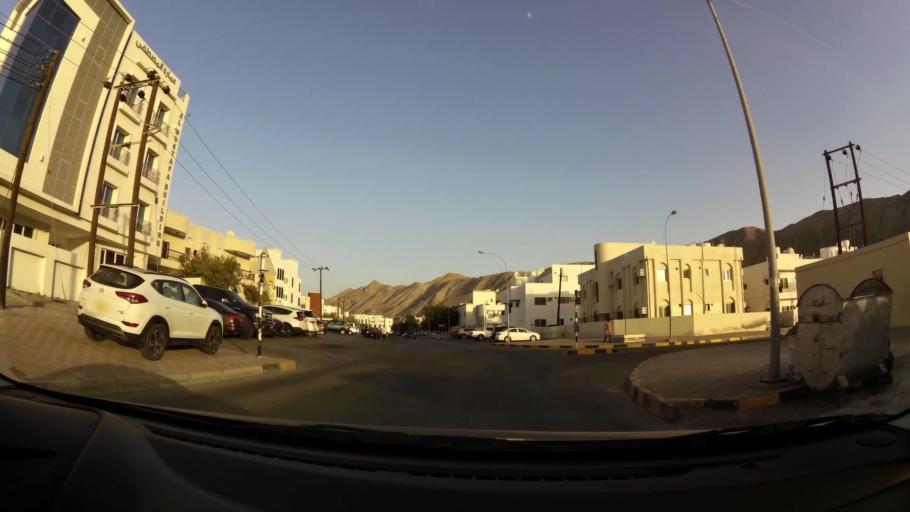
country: OM
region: Muhafazat Masqat
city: Muscat
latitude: 23.5741
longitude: 58.5711
